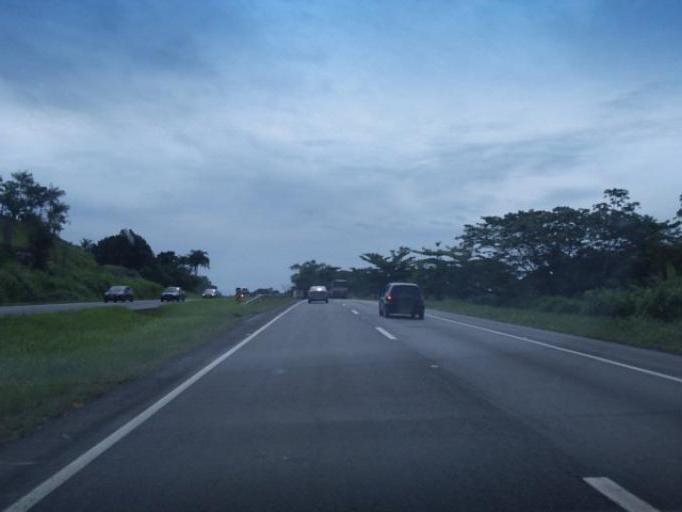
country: BR
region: Sao Paulo
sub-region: Miracatu
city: Miracatu
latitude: -24.3095
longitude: -47.5064
